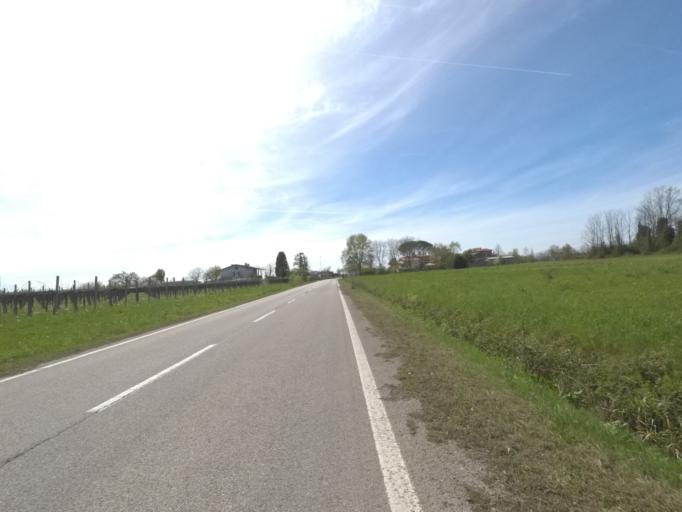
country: IT
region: Friuli Venezia Giulia
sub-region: Provincia di Pordenone
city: Castions
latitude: 45.9460
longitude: 12.8054
